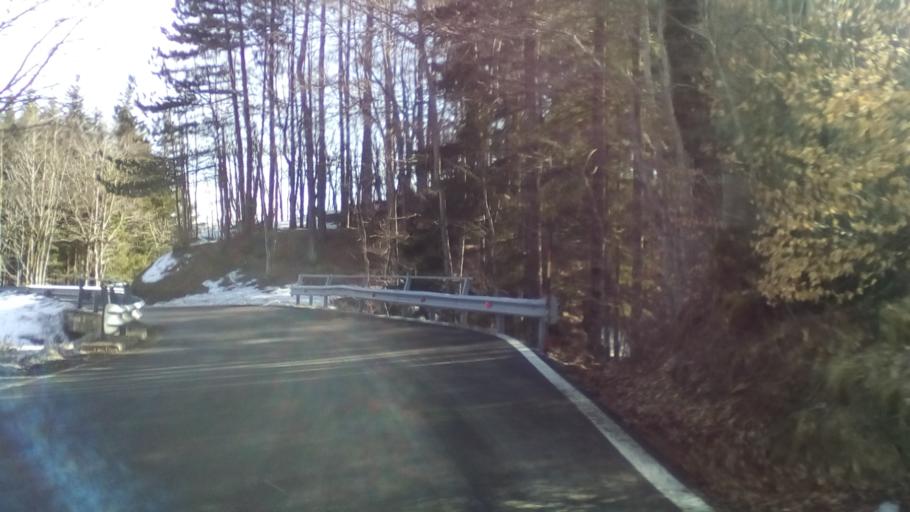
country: IT
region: Emilia-Romagna
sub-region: Provincia di Modena
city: Pievepelago
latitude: 44.1979
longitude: 10.5242
